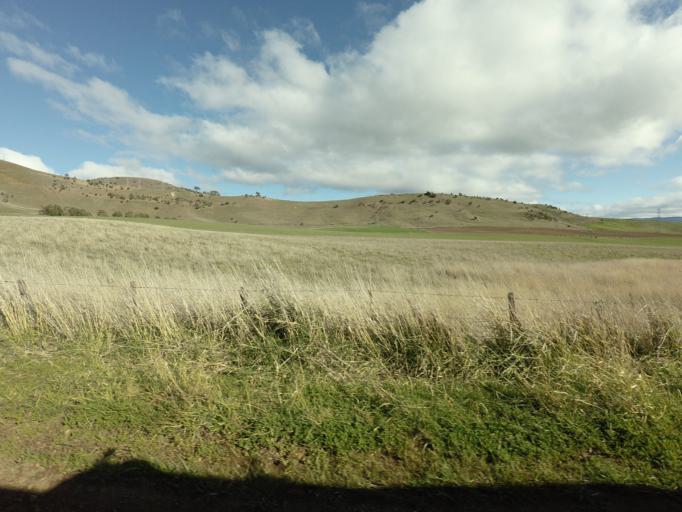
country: AU
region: Tasmania
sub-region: Derwent Valley
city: New Norfolk
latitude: -42.6967
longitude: 146.9730
